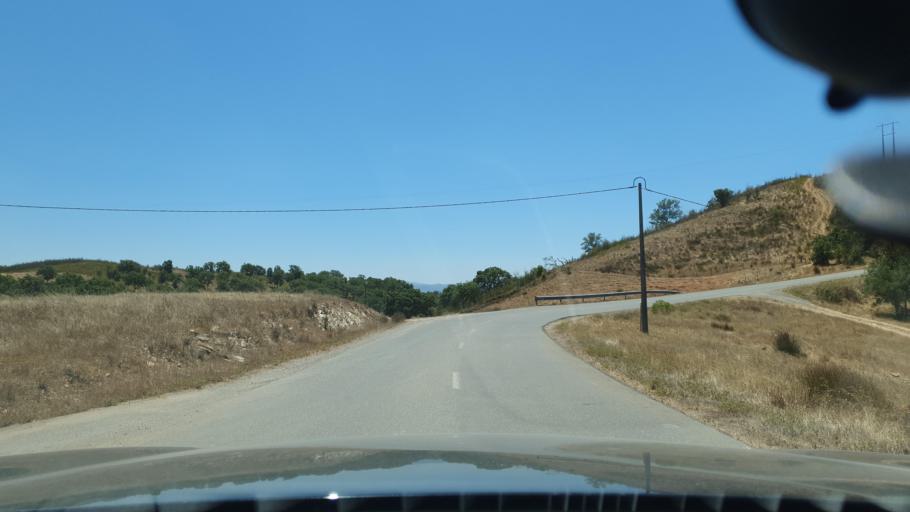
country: PT
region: Beja
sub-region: Odemira
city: Odemira
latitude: 37.5517
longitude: -8.4358
